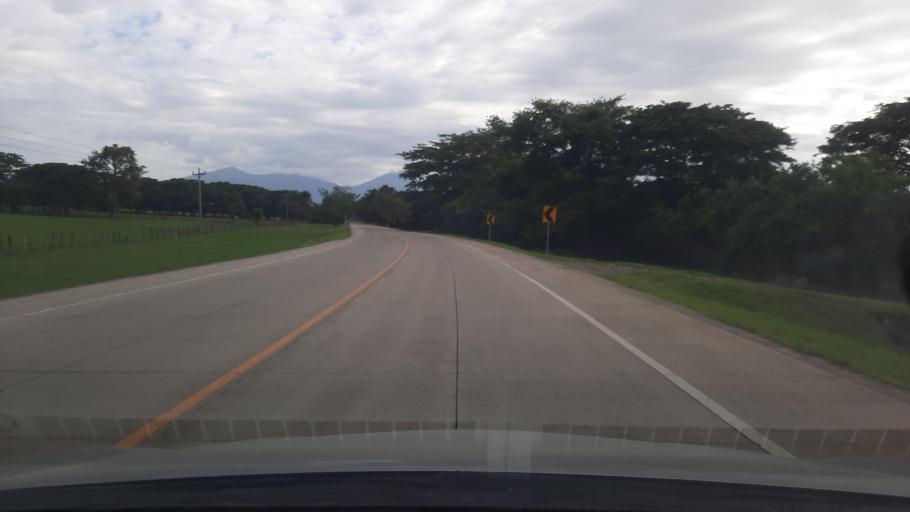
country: NI
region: Chinandega
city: Somotillo
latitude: 12.8604
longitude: -86.8672
